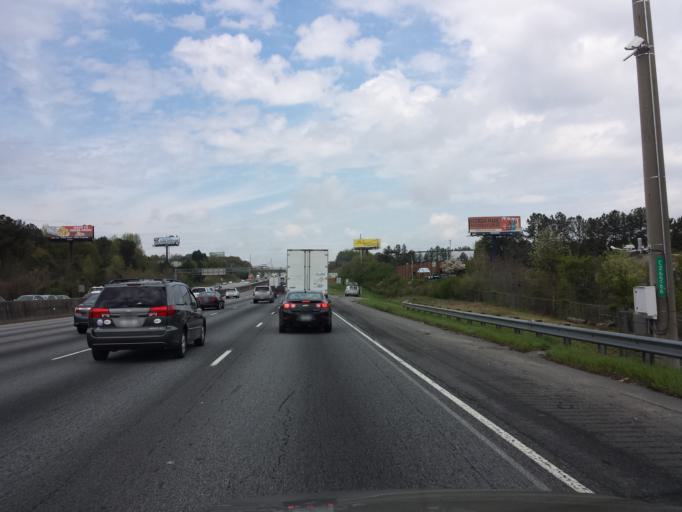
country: US
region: Georgia
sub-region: Cobb County
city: Marietta
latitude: 33.9688
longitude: -84.5265
